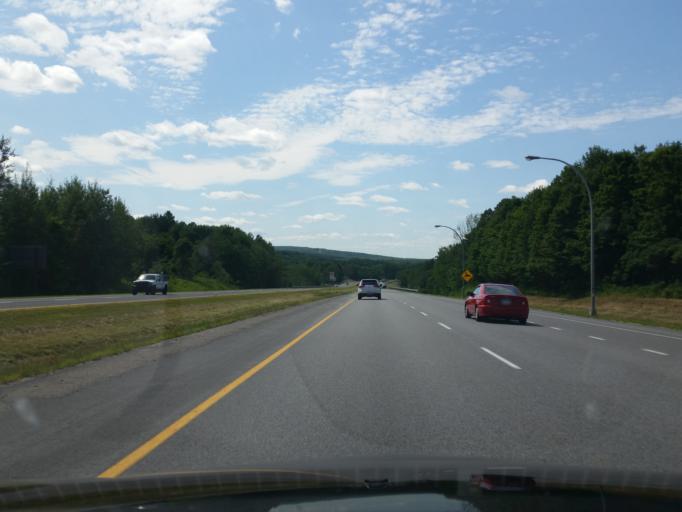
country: CA
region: Quebec
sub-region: Monteregie
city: Hudson
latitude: 45.4365
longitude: -74.1800
